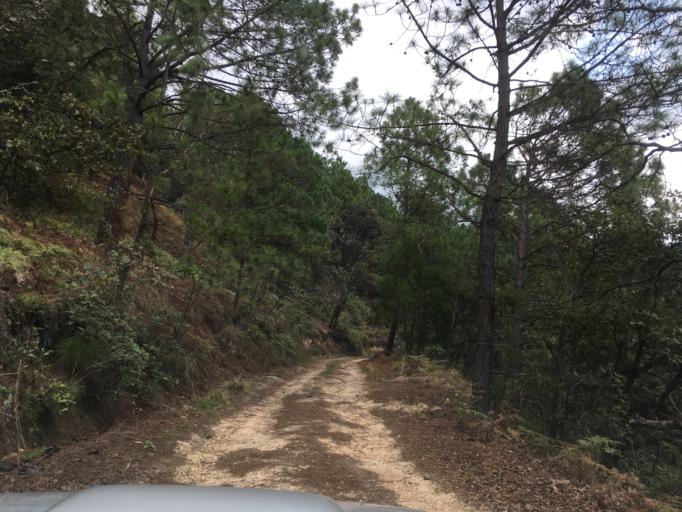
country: MX
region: Michoacan
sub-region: Zitacuaro
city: Macutzio
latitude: 19.5041
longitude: -100.3282
